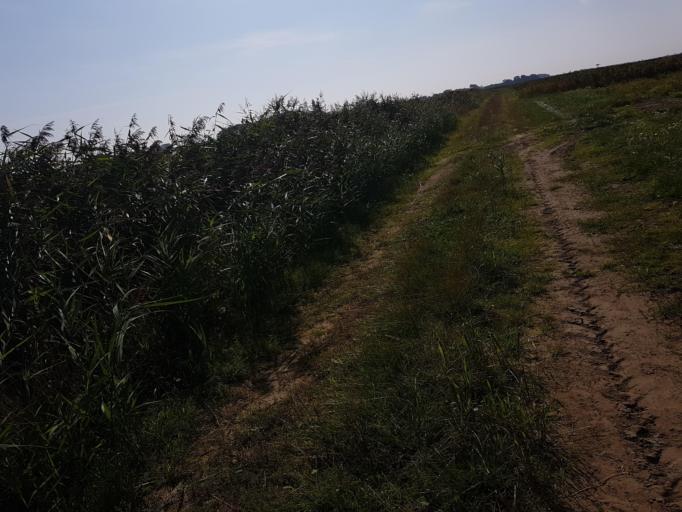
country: NL
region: North Holland
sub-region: Gemeente Texel
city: Den Burg
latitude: 53.0997
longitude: 4.8750
